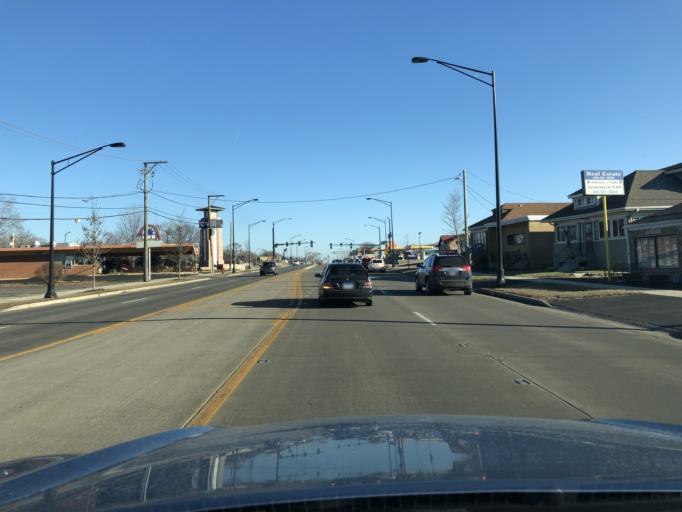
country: US
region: Illinois
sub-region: DuPage County
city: Wood Dale
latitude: 41.9637
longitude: -87.9811
